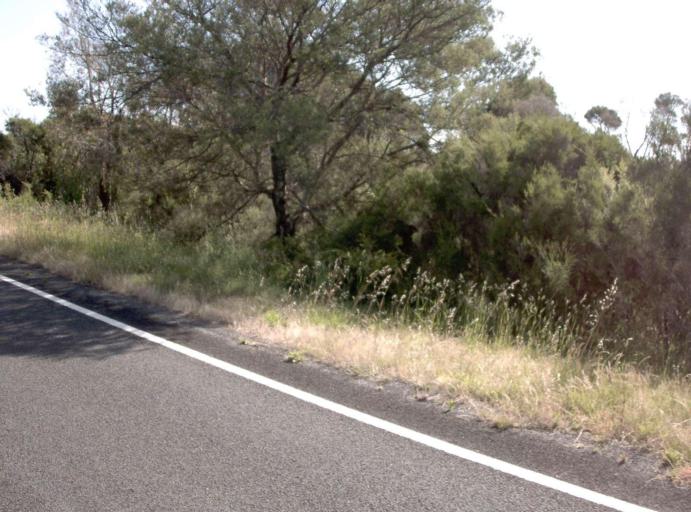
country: AU
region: Victoria
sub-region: Cardinia
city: Koo-Wee-Rup
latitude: -38.2978
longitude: 145.5443
